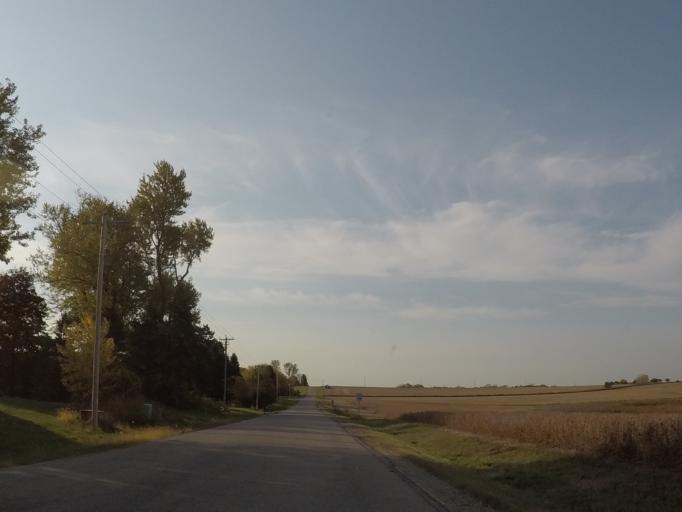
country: US
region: Wisconsin
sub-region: Dane County
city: Cross Plains
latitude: 43.0571
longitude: -89.6010
